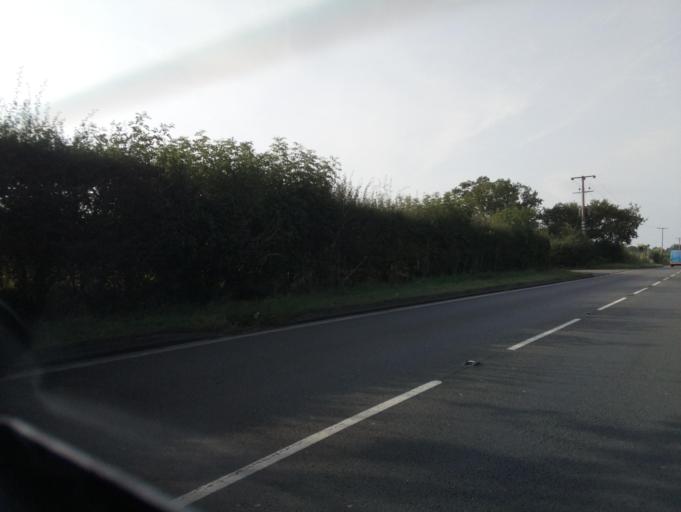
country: GB
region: England
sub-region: Warwickshire
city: Alcester
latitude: 52.2346
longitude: -1.8816
